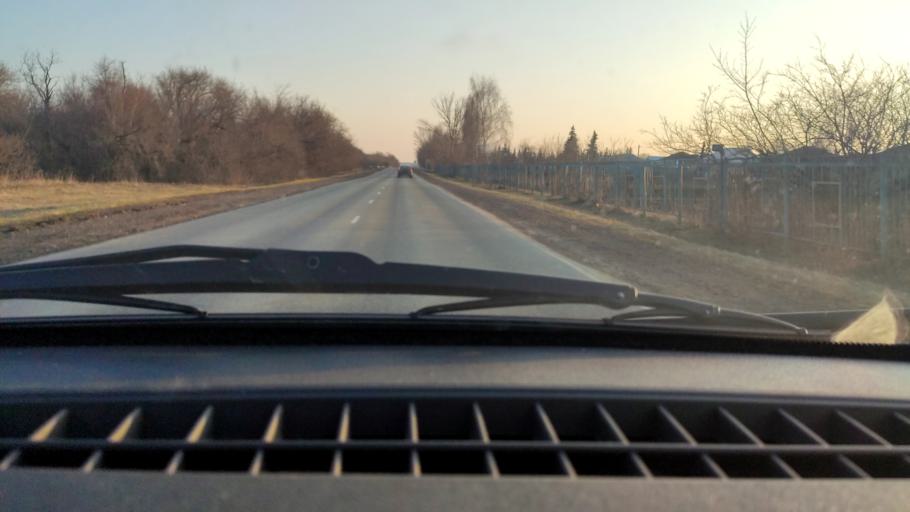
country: RU
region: Bashkortostan
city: Davlekanovo
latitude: 54.2974
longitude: 55.1284
